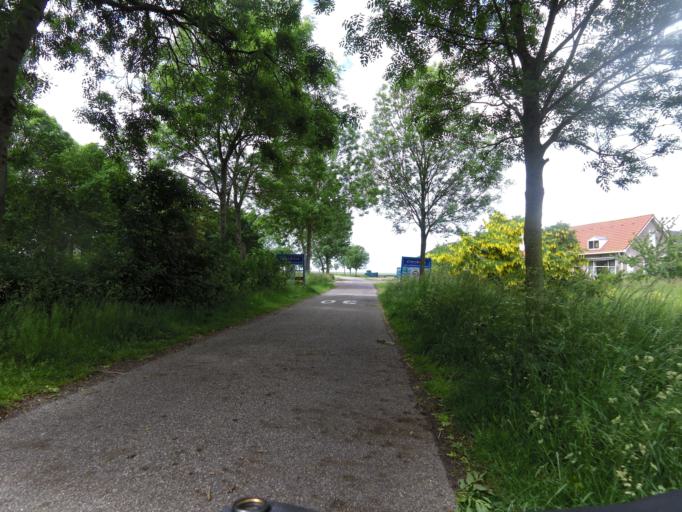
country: NL
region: Zeeland
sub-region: Schouwen-Duiveland
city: Scharendijke
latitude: 51.6547
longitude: 3.9041
